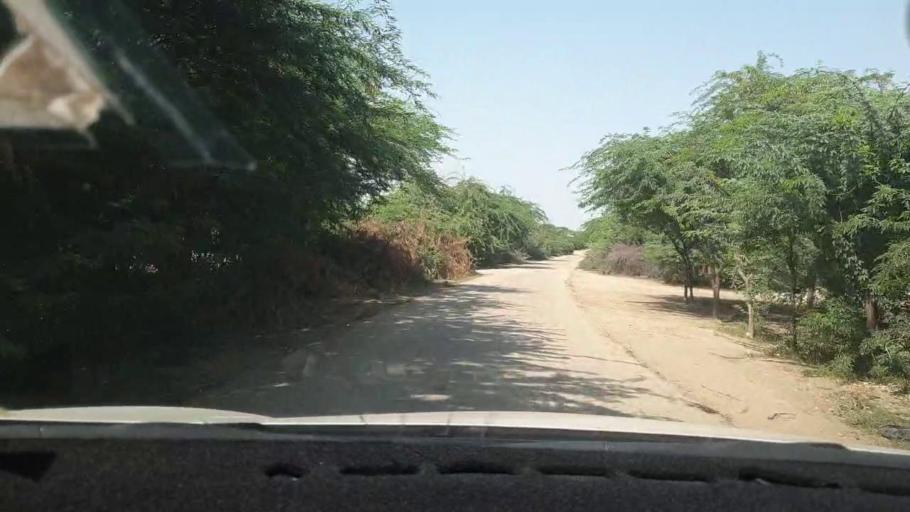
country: PK
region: Sindh
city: Tando Mittha Khan
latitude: 25.8773
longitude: 69.3870
